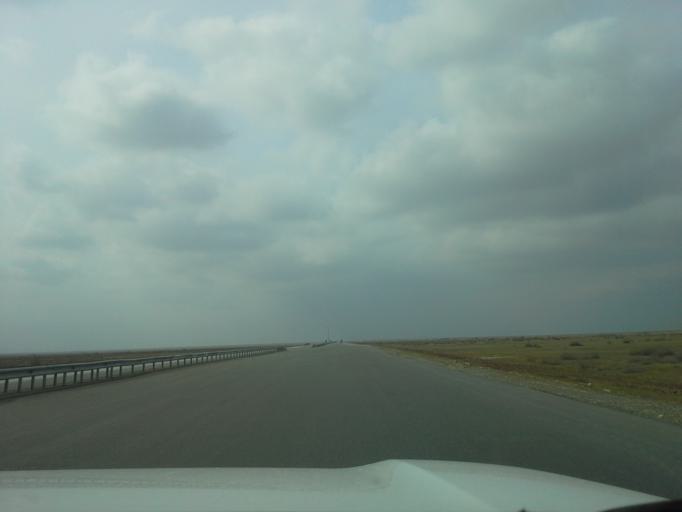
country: IR
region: Razavi Khorasan
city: Kalat-e Naderi
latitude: 37.2228
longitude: 59.9747
